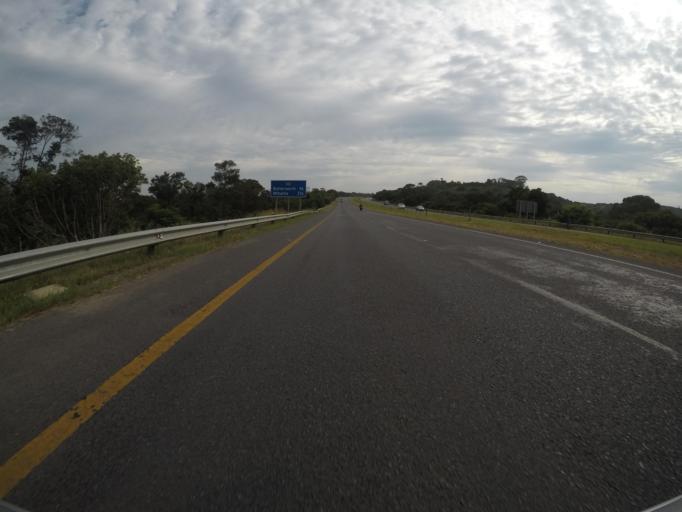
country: ZA
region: Eastern Cape
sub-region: Buffalo City Metropolitan Municipality
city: East London
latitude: -32.9451
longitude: 27.9415
